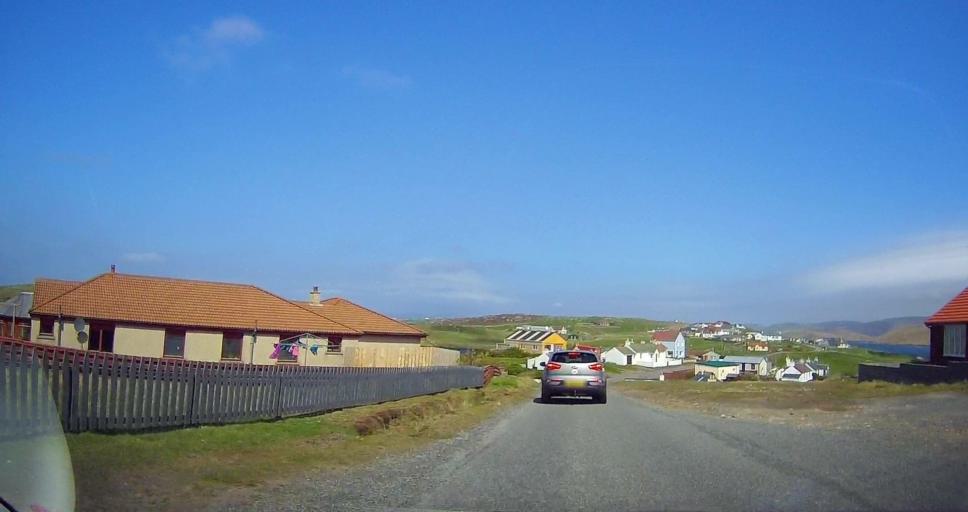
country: GB
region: Scotland
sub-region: Shetland Islands
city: Sandwick
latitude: 60.0799
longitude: -1.3375
